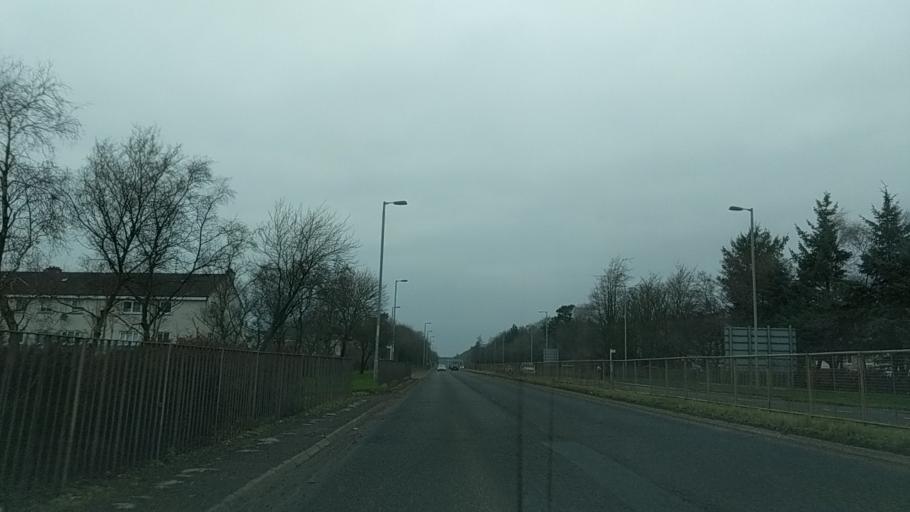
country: GB
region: Scotland
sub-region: South Lanarkshire
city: East Kilbride
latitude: 55.7605
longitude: -4.1884
